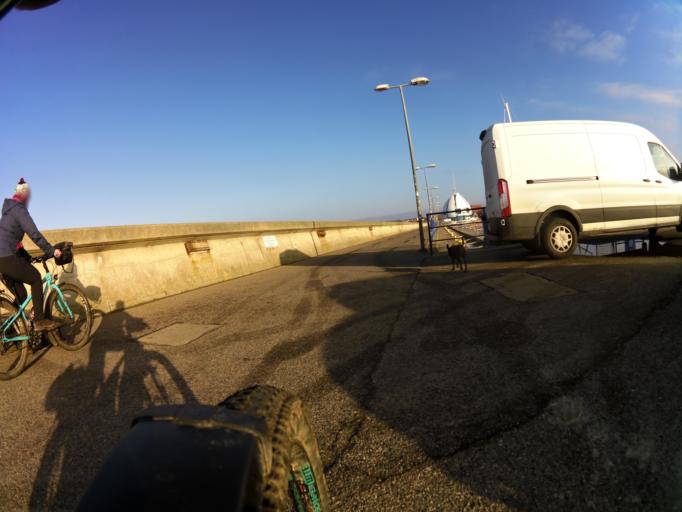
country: PL
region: Pomeranian Voivodeship
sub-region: Powiat pucki
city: Hel
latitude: 54.6014
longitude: 18.7991
